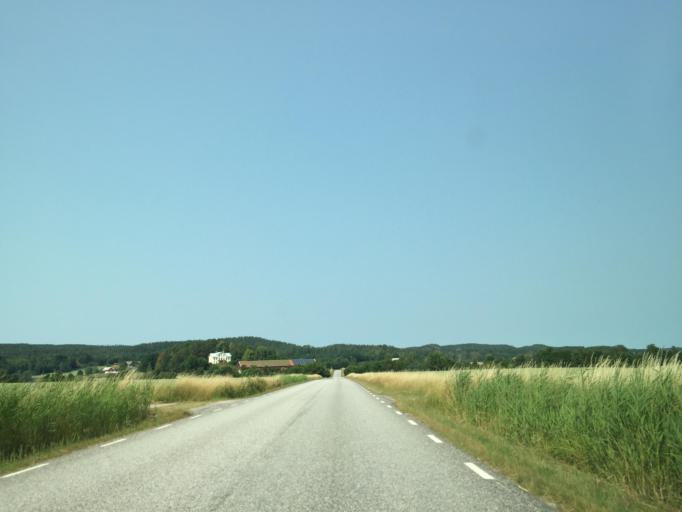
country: SE
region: Vaestra Goetaland
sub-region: Lilla Edets Kommun
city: Lilla Edet
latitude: 58.1916
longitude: 12.1176
